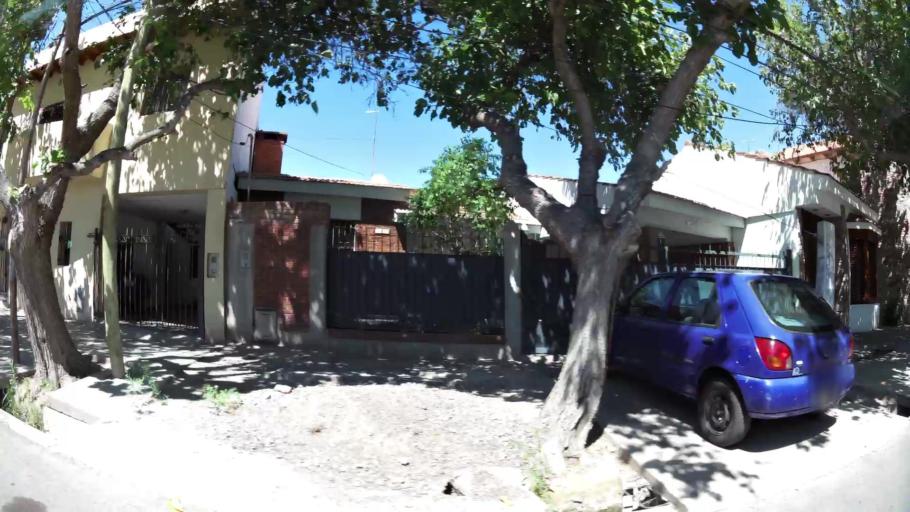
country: AR
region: San Juan
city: San Juan
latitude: -31.5237
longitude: -68.5445
